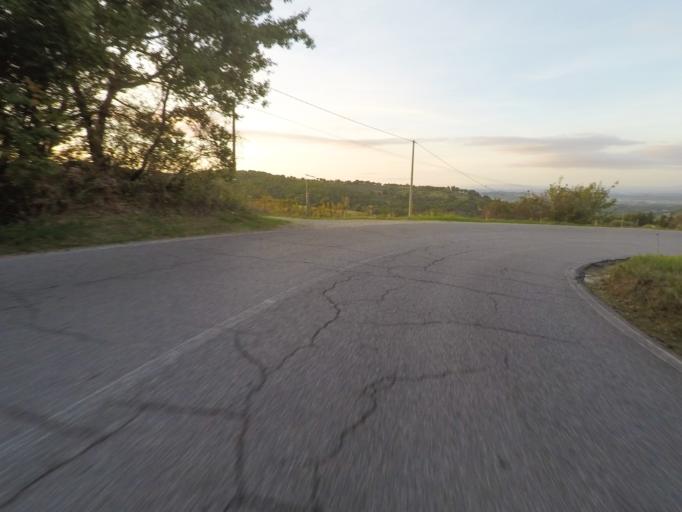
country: IT
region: Tuscany
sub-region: Provincia di Siena
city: Torrita di Siena
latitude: 43.1475
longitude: 11.7377
